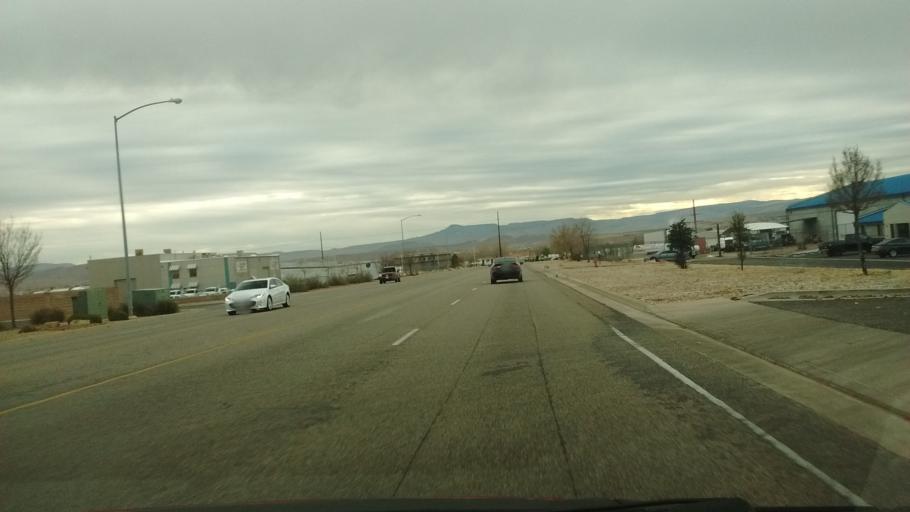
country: US
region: Utah
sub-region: Washington County
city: Washington
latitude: 37.1139
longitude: -113.5207
